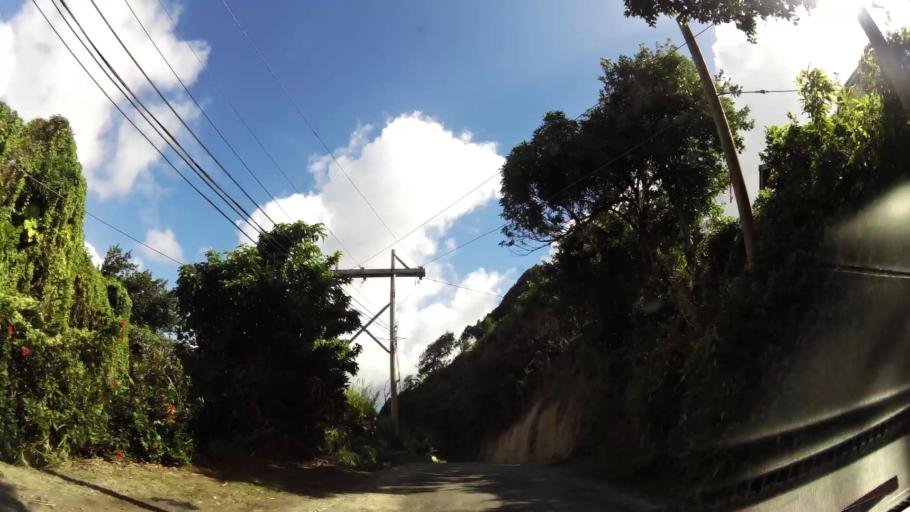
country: DM
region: Saint Andrew
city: Calibishie
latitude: 15.6046
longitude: -61.3993
